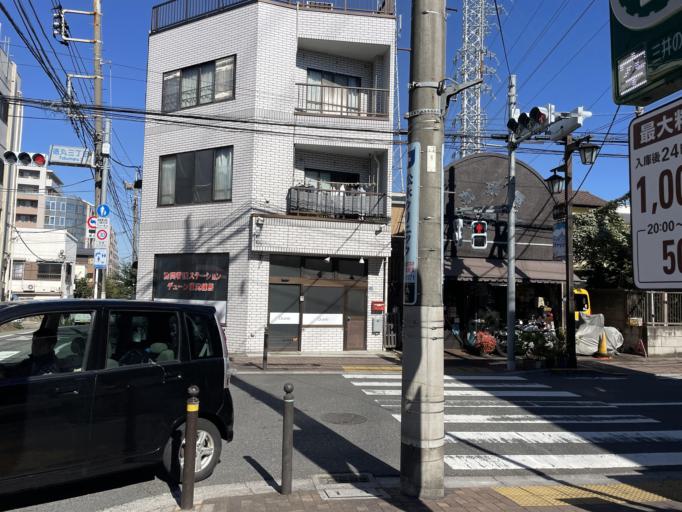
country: JP
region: Saitama
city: Wako
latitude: 35.7711
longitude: 139.6572
